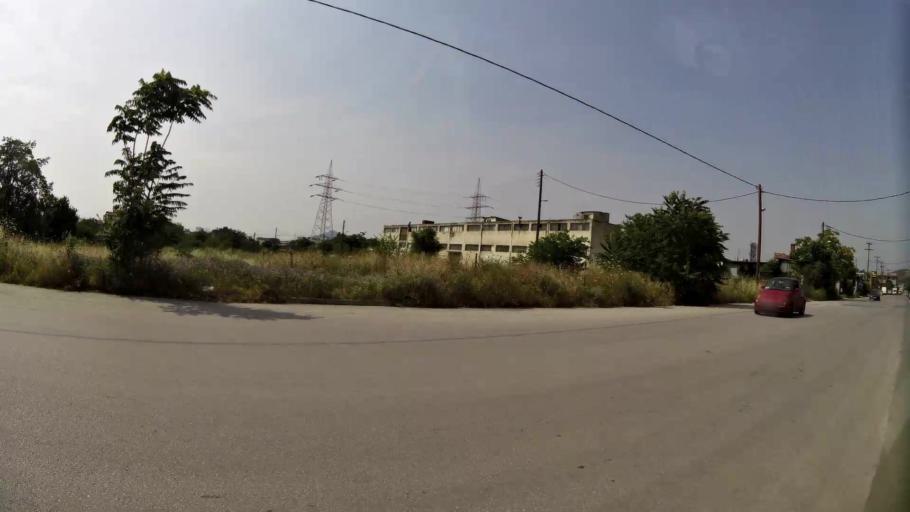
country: GR
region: Central Macedonia
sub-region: Nomos Thessalonikis
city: Efkarpia
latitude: 40.6878
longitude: 22.9479
